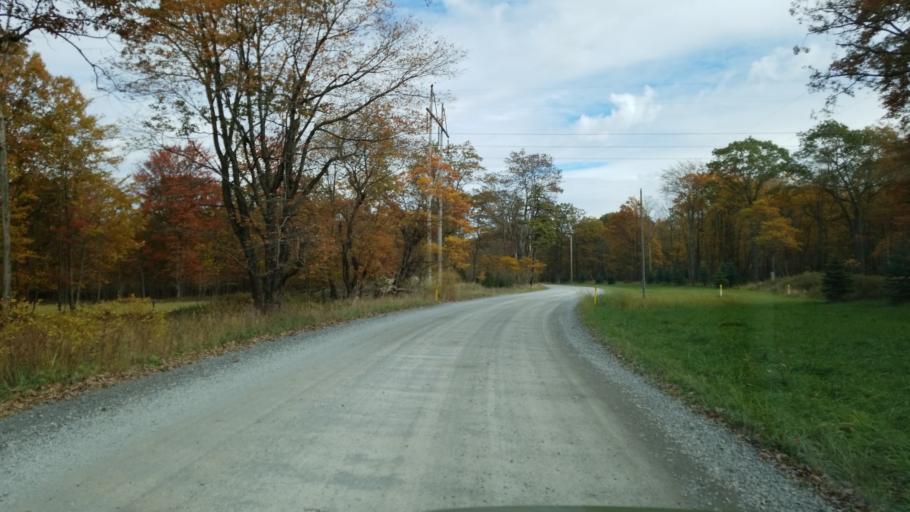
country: US
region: Pennsylvania
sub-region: Clearfield County
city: Clearfield
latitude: 41.1542
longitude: -78.4630
